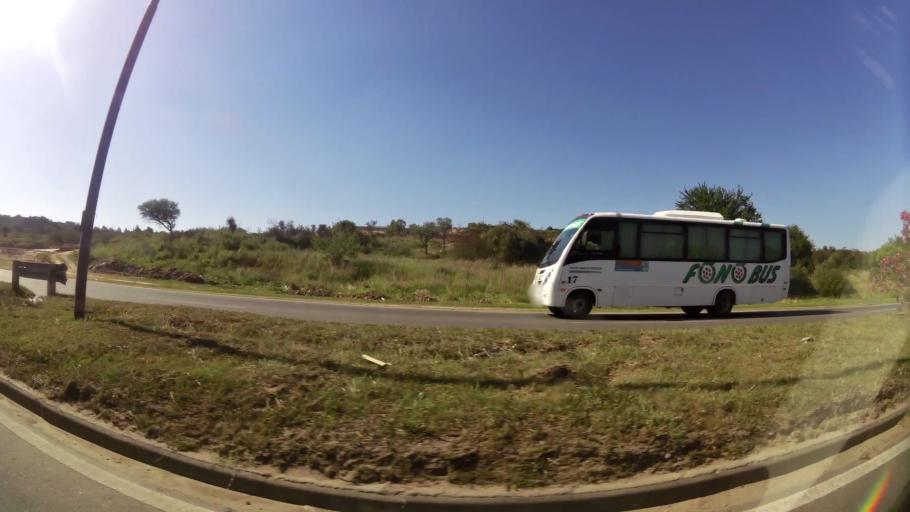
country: AR
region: Cordoba
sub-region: Departamento de Capital
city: Cordoba
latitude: -31.3990
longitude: -64.1414
